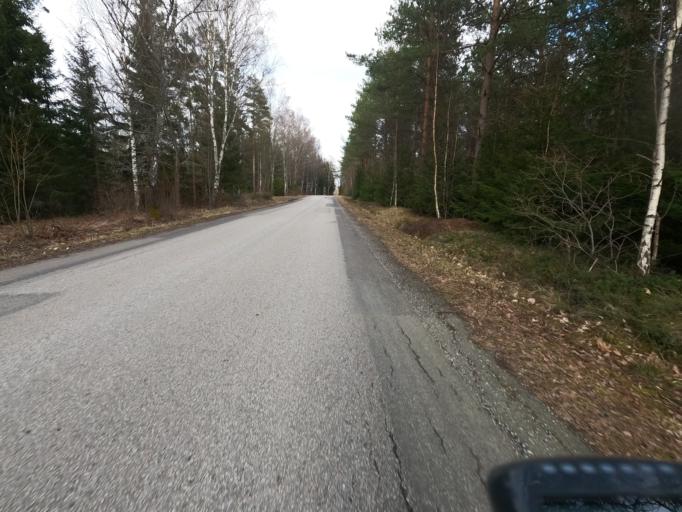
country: SE
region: Kronoberg
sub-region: Alvesta Kommun
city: Vislanda
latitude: 56.8151
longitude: 14.5028
